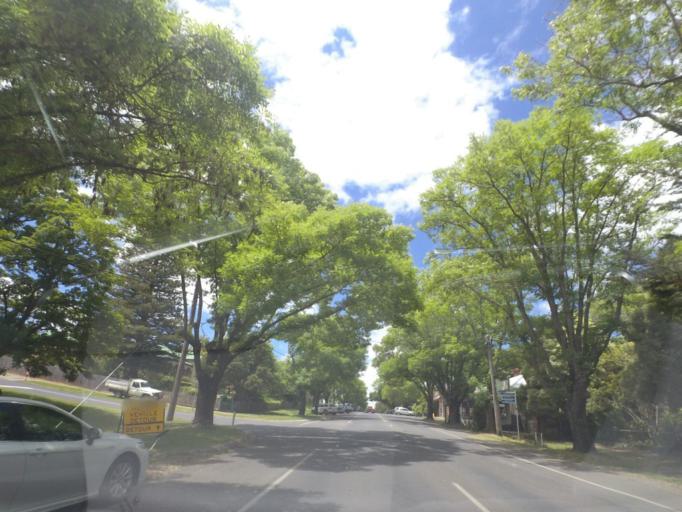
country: AU
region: Victoria
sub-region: Mount Alexander
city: Castlemaine
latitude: -37.3402
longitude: 144.1499
